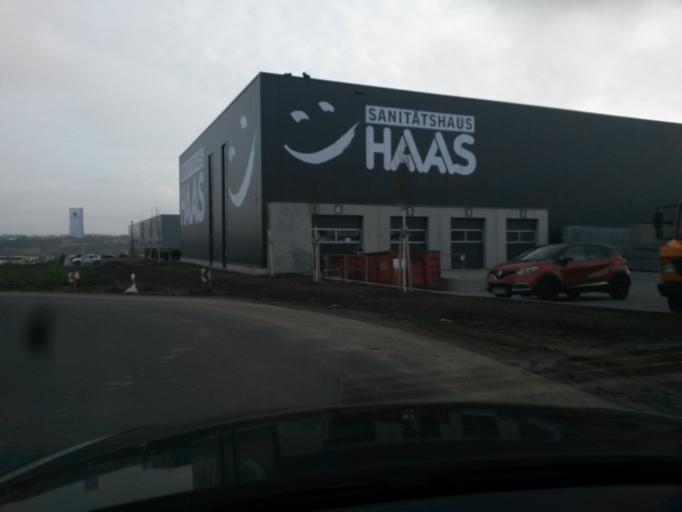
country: DE
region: Bavaria
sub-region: Regierungsbezirk Unterfranken
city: Estenfeld
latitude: 49.8403
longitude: 10.0083
